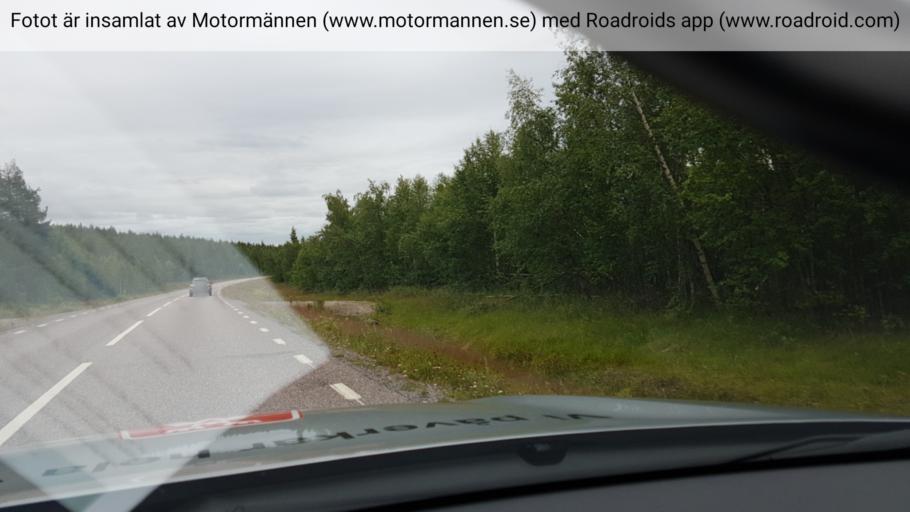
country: SE
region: Norrbotten
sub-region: Gallivare Kommun
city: Gaellivare
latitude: 67.0381
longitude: 21.6703
